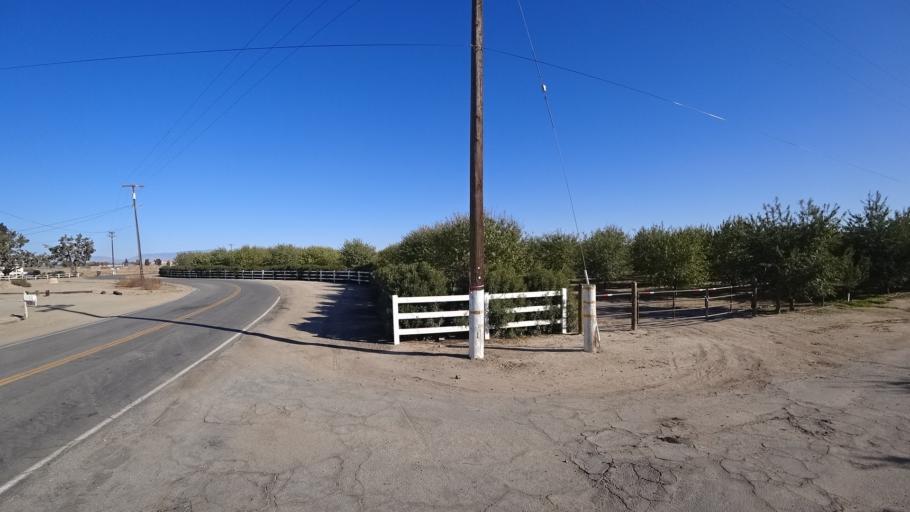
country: US
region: California
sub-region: Kern County
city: Greenacres
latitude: 35.2812
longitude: -119.1187
